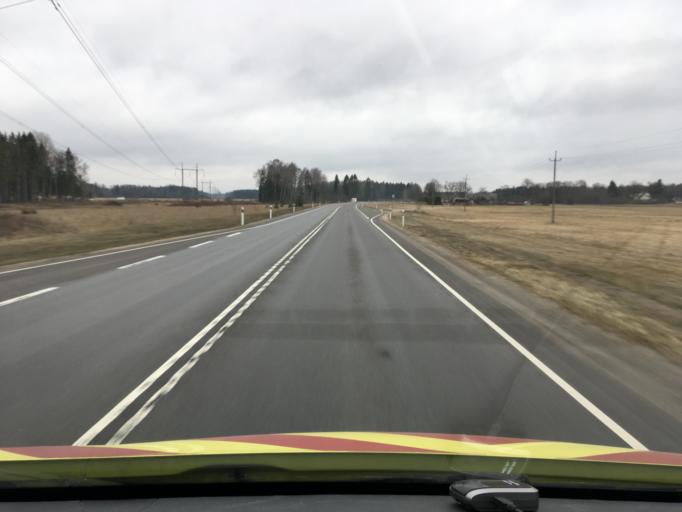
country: EE
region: Raplamaa
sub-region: Kohila vald
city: Kohila
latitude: 59.2137
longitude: 24.7772
